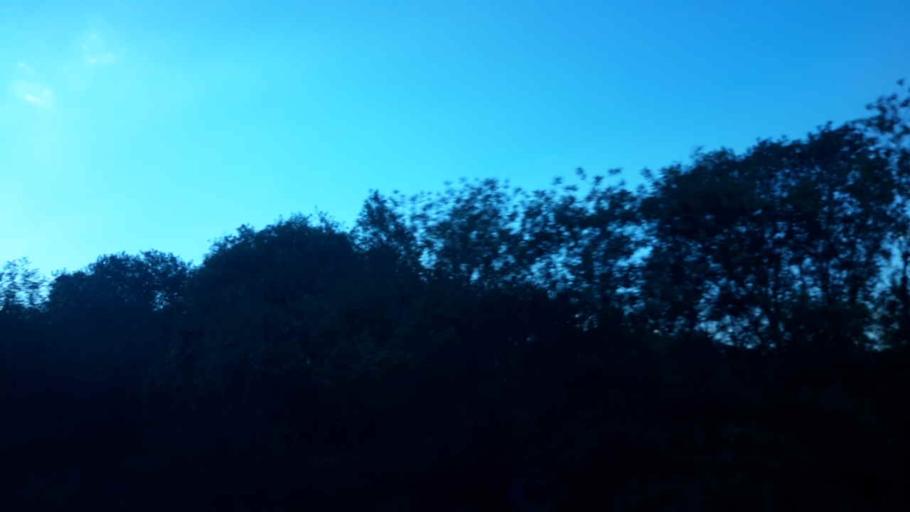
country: AU
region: New South Wales
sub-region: Camden
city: Camden South
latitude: -34.1242
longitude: 150.6970
